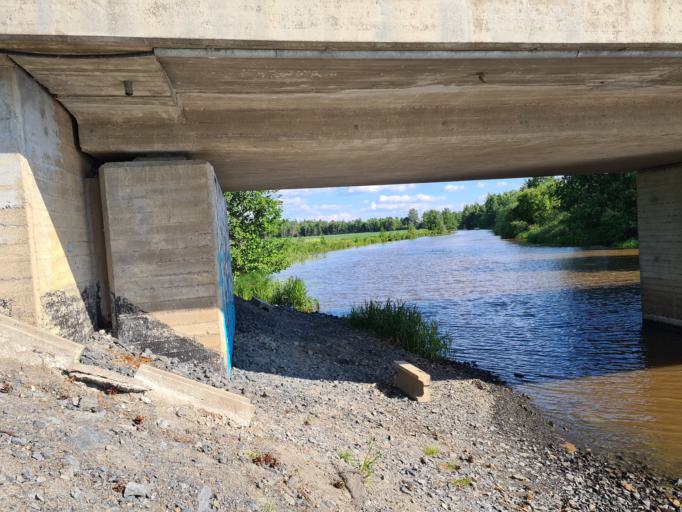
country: FI
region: Haeme
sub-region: Forssa
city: Tammela
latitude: 60.8021
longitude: 23.6949
